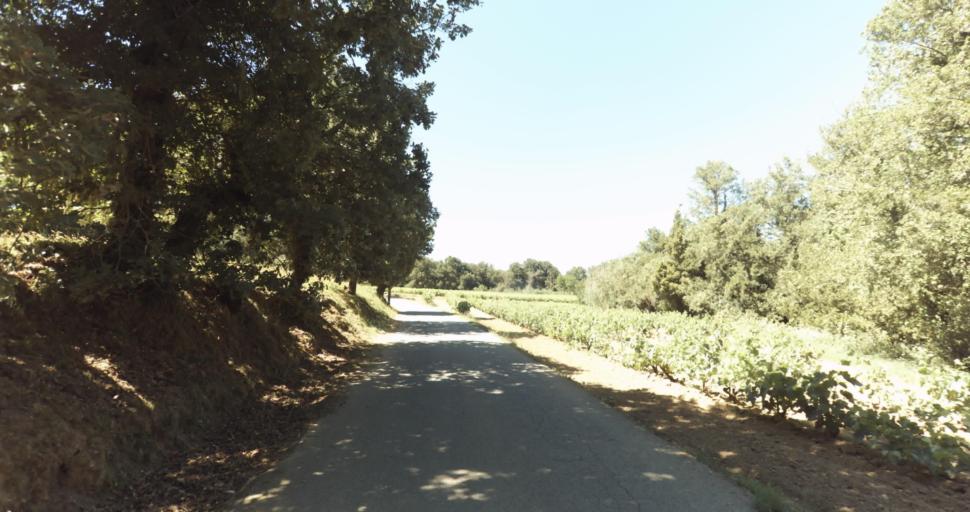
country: FR
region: Provence-Alpes-Cote d'Azur
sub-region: Departement du Var
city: Gassin
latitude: 43.2310
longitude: 6.5674
